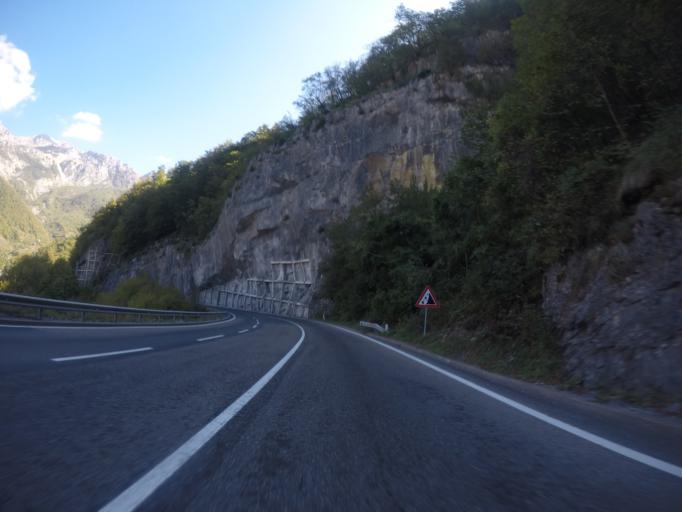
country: ME
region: Opstina Kolasin
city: Kolasin
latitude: 42.8122
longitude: 19.3986
